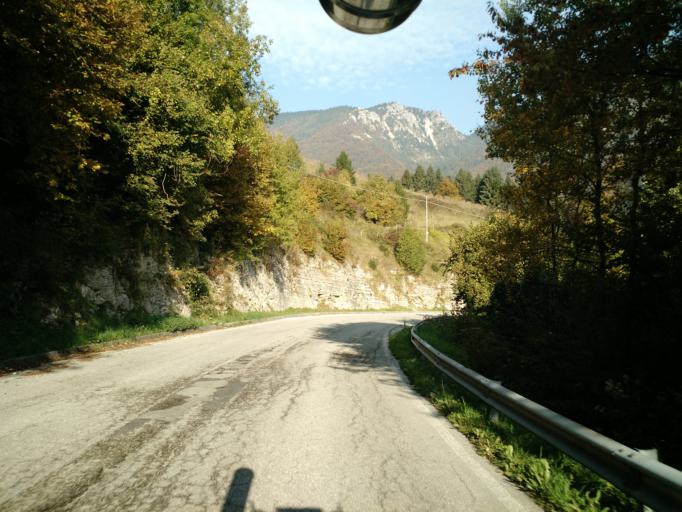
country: IT
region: Veneto
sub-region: Provincia di Vicenza
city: Foza
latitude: 45.8852
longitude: 11.6077
